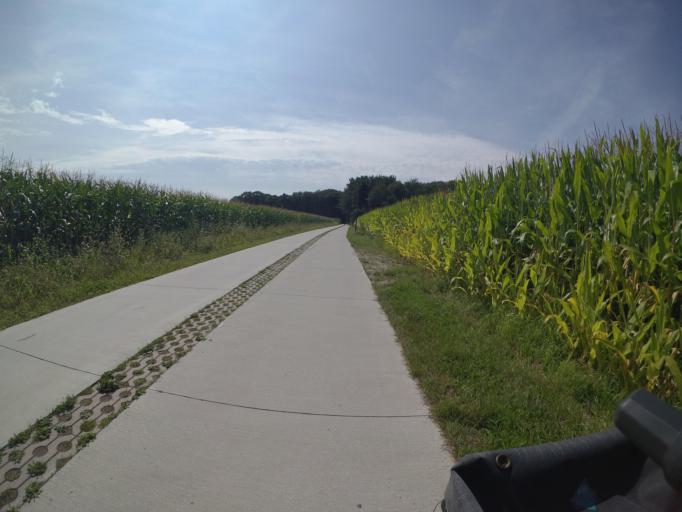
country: NL
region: North Brabant
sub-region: Bergeijk
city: Bergeyk
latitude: 51.3322
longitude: 5.3649
